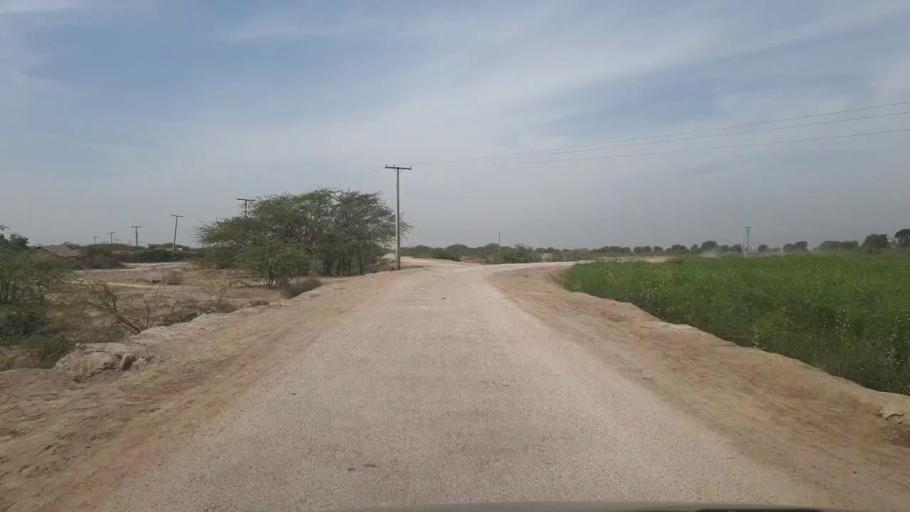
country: PK
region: Sindh
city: Kunri
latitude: 25.2290
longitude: 69.6727
